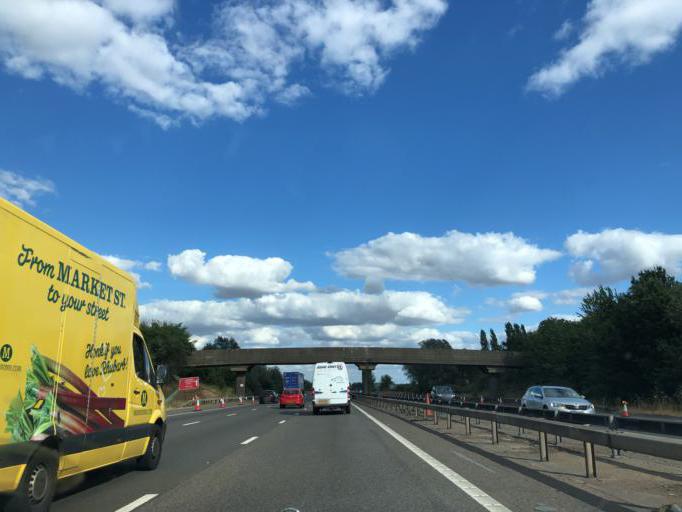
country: GB
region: England
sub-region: Central Bedfordshire
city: Aspley Guise
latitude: 52.0337
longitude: -0.6322
